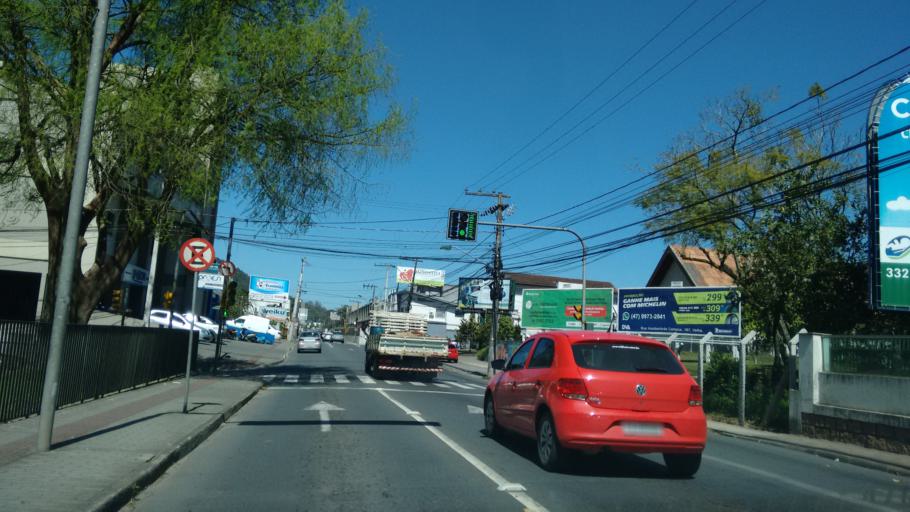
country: BR
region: Santa Catarina
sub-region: Blumenau
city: Blumenau
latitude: -26.8935
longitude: -49.0850
